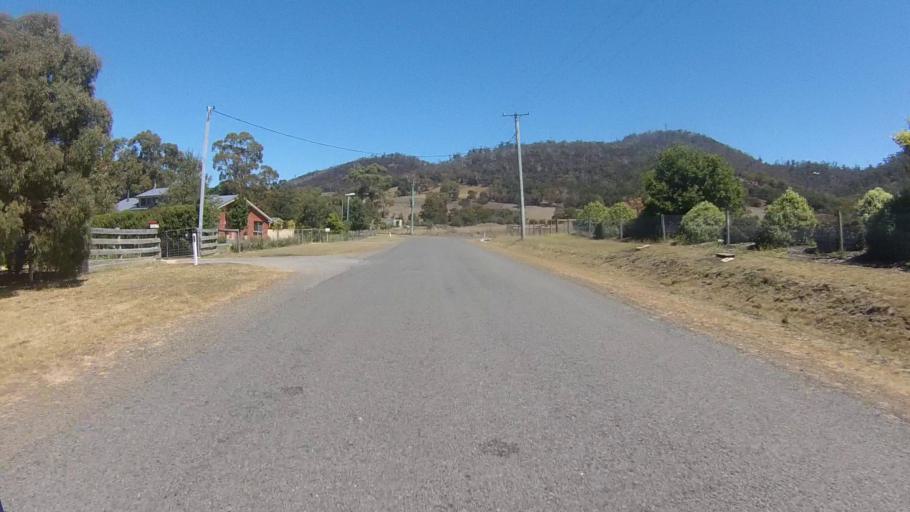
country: AU
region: Tasmania
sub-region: Clarence
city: Cambridge
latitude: -42.8491
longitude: 147.4633
